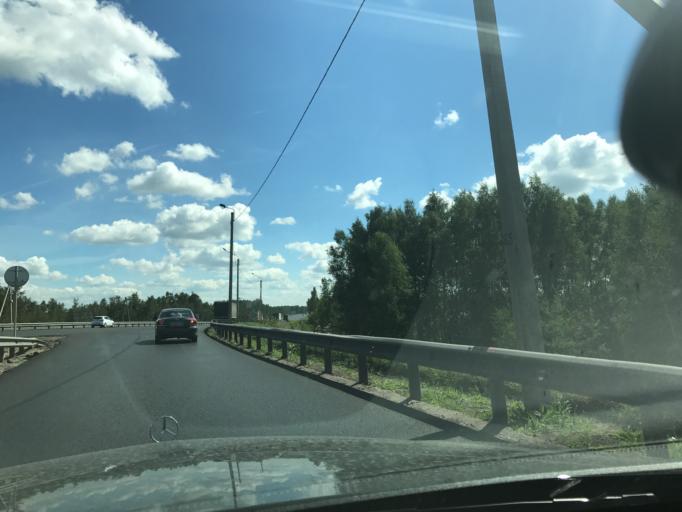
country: RU
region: Nizjnij Novgorod
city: Gorbatovka
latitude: 56.3036
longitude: 43.6859
